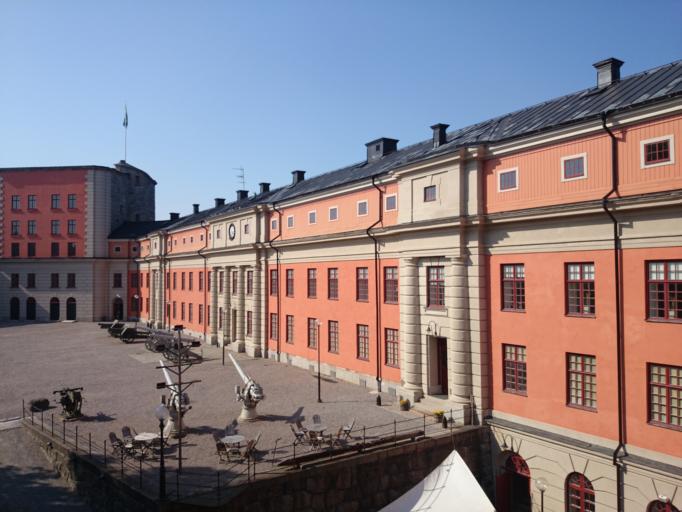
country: SE
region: Stockholm
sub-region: Vaxholms Kommun
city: Vaxholm
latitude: 59.4030
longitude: 18.3601
